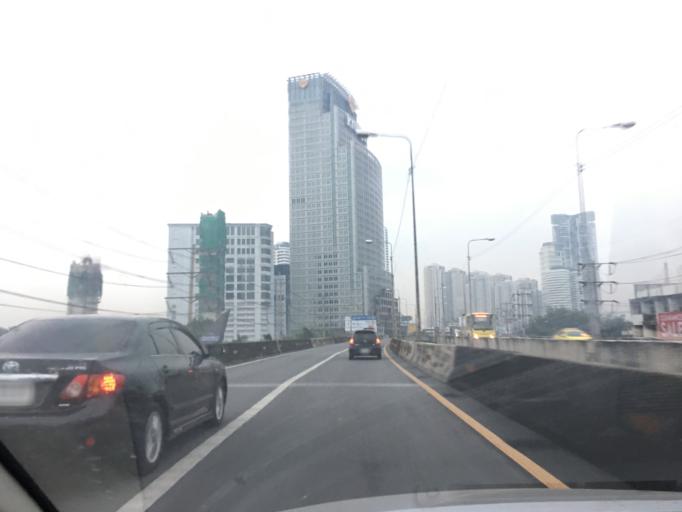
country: TH
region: Bangkok
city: Yan Nawa
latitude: 13.6802
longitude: 100.5475
